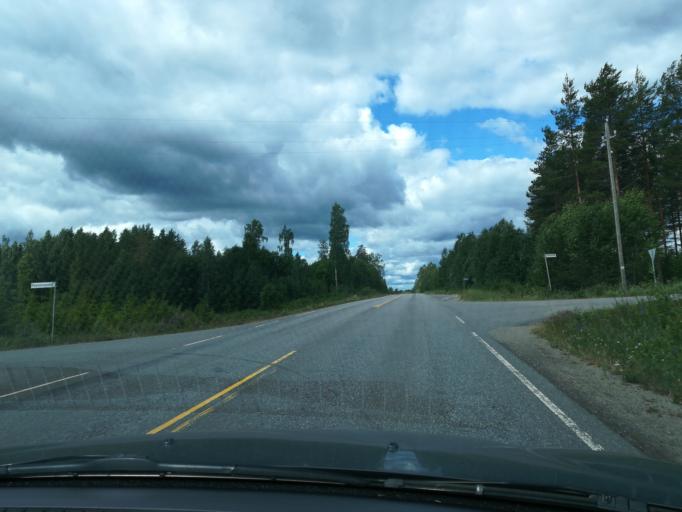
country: FI
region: Southern Savonia
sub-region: Mikkeli
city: Maentyharju
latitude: 61.3648
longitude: 26.9517
